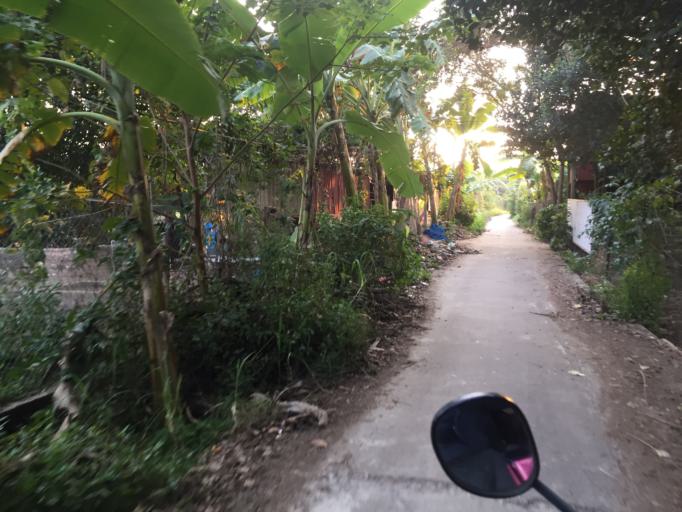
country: VN
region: Ha Noi
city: Chuc Son
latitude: 20.9073
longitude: 105.7293
